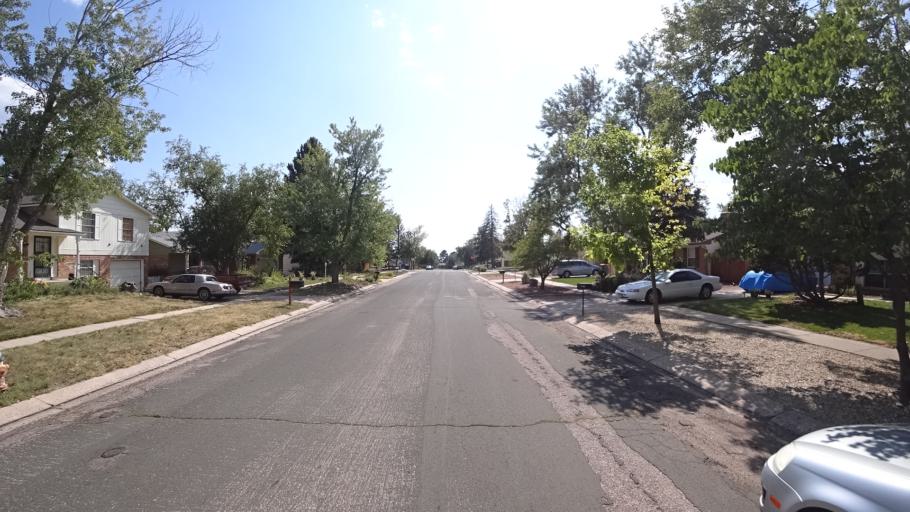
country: US
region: Colorado
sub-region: El Paso County
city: Colorado Springs
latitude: 38.8495
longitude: -104.7655
